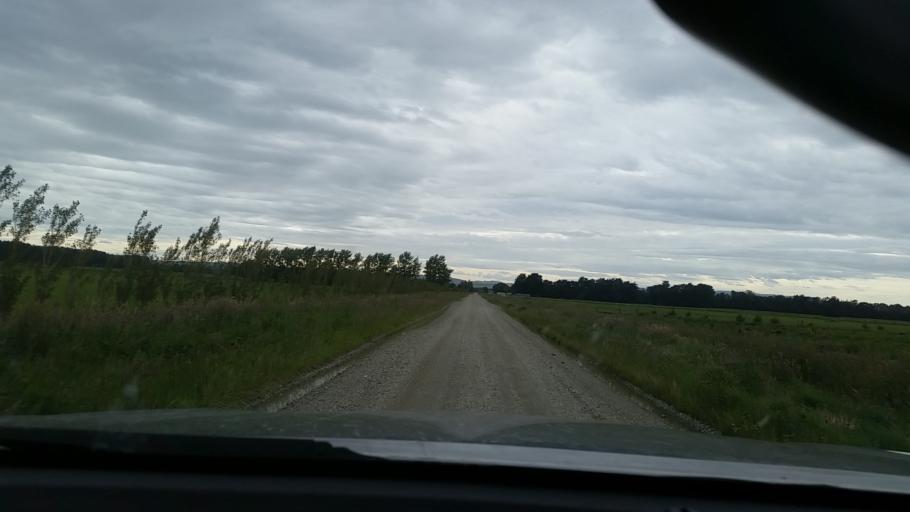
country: NZ
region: Southland
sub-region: Gore District
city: Gore
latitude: -46.2842
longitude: 168.7682
